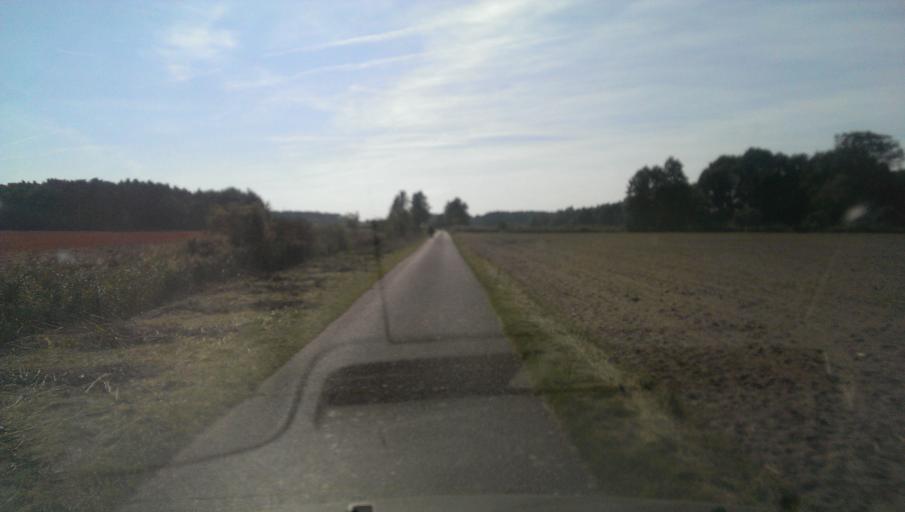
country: DE
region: Brandenburg
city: Am Mellensee
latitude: 52.2022
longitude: 13.3376
